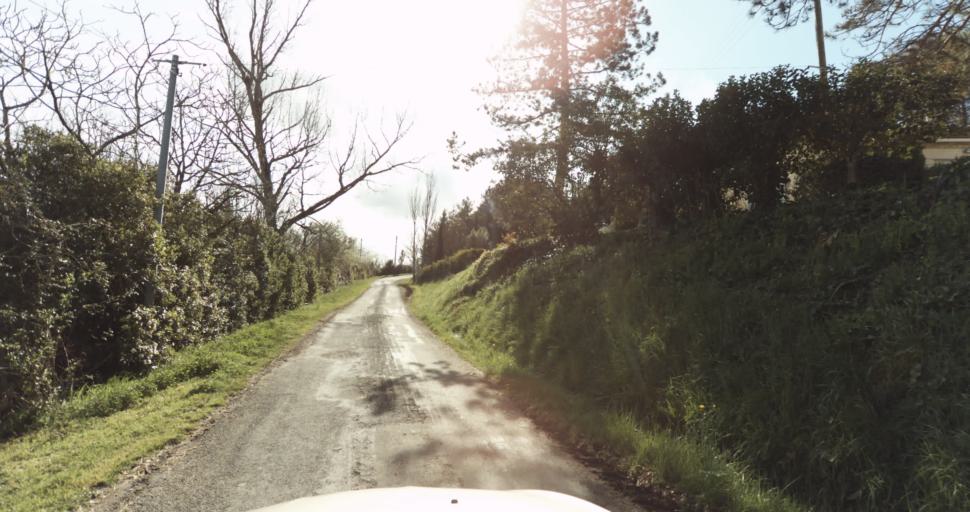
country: FR
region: Midi-Pyrenees
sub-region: Departement du Tarn
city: Puygouzon
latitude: 43.8689
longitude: 2.1724
